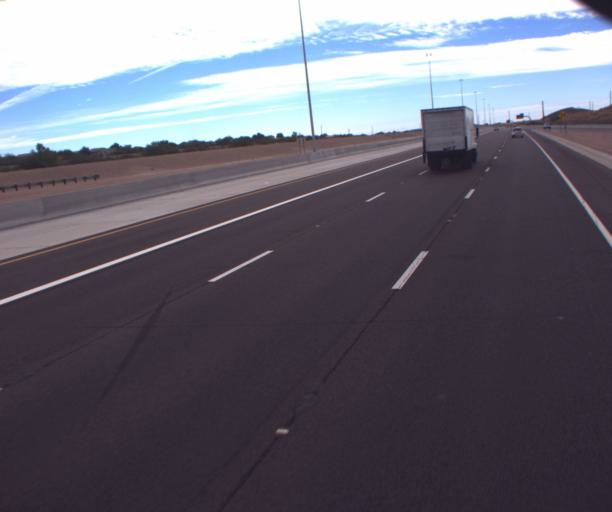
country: US
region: Arizona
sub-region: Pinal County
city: Apache Junction
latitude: 33.4638
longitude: -111.6787
